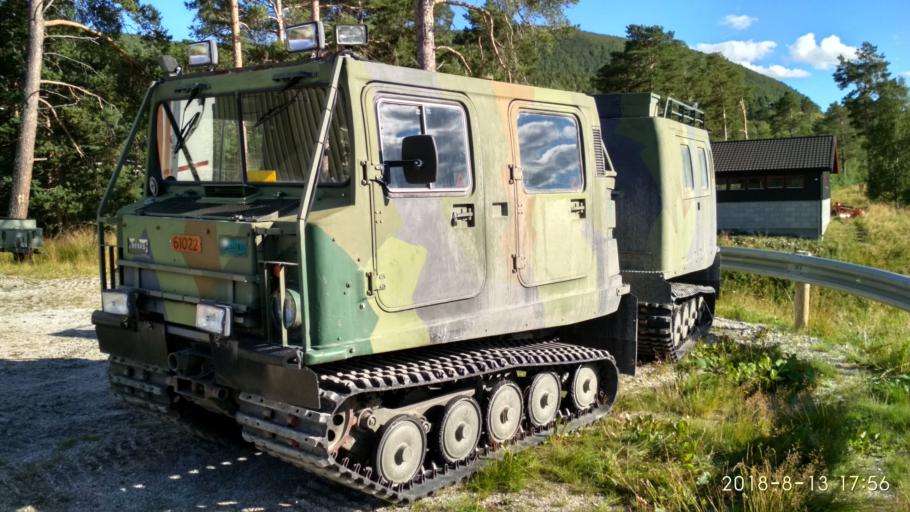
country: NO
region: Oppland
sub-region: Dovre
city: Dombas
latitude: 62.0775
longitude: 9.1302
